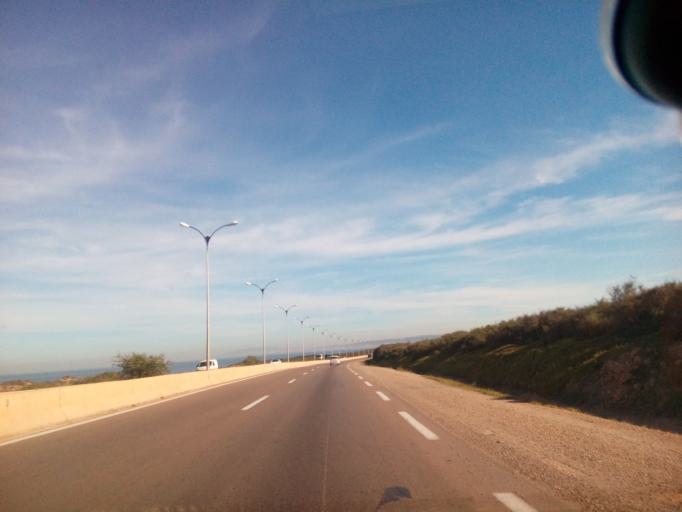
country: DZ
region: Oran
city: Ain el Bya
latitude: 35.7961
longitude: -0.0891
